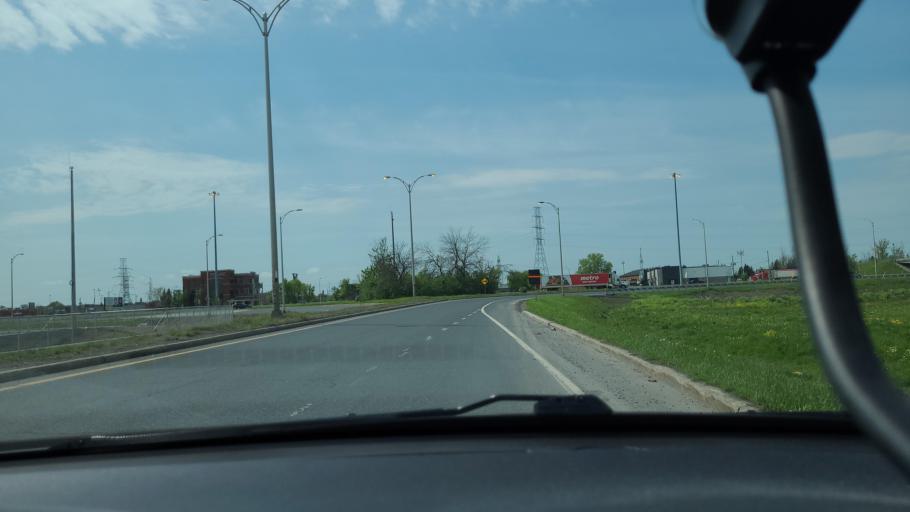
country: CA
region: Quebec
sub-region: Monteregie
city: Boucherville
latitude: 45.5736
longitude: -73.4461
